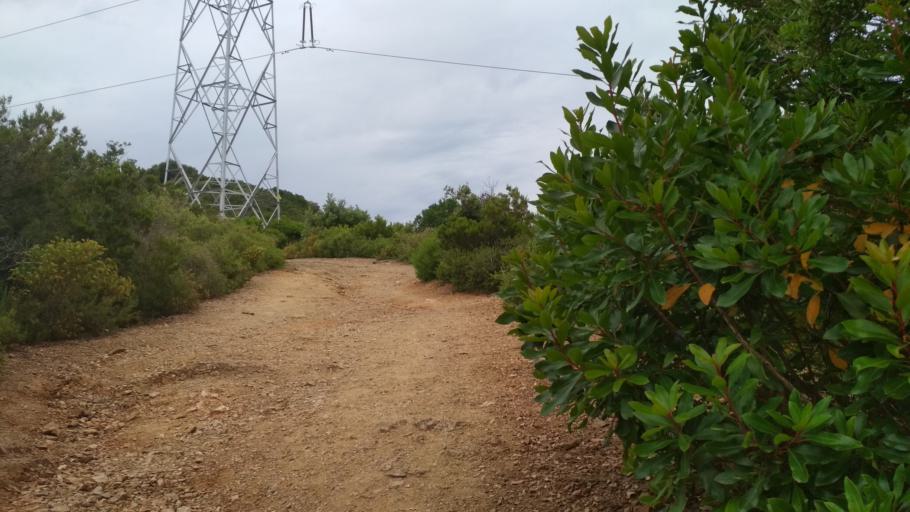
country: ES
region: Catalonia
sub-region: Provincia de Barcelona
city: Horta-Guinardo
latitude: 41.4427
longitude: 2.1400
